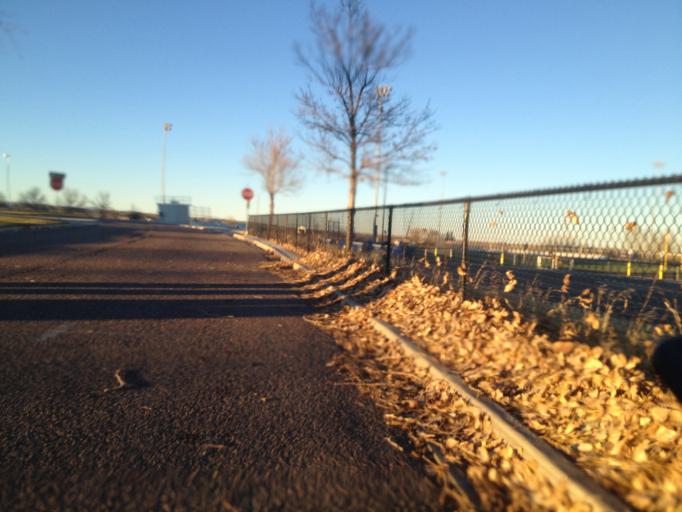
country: US
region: Colorado
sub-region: Boulder County
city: Louisville
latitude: 39.9512
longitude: -105.1391
